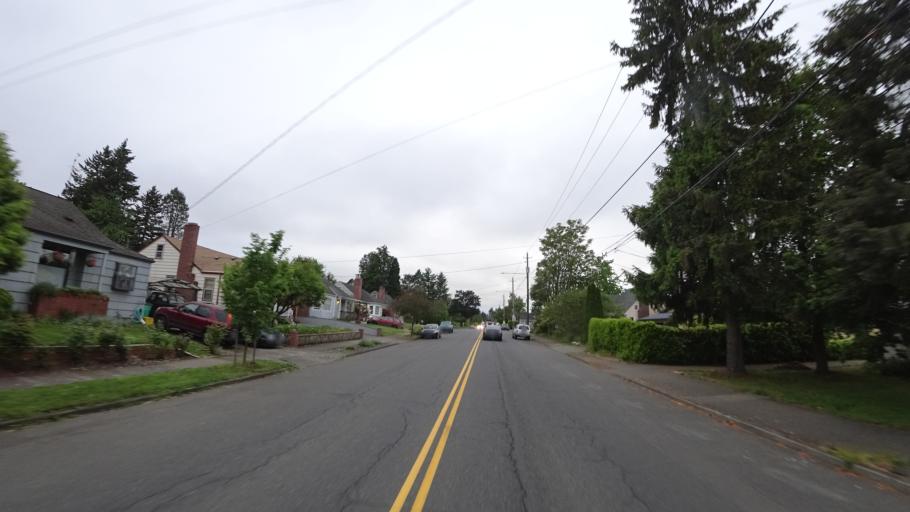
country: US
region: Oregon
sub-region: Multnomah County
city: Portland
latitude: 45.5555
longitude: -122.6159
